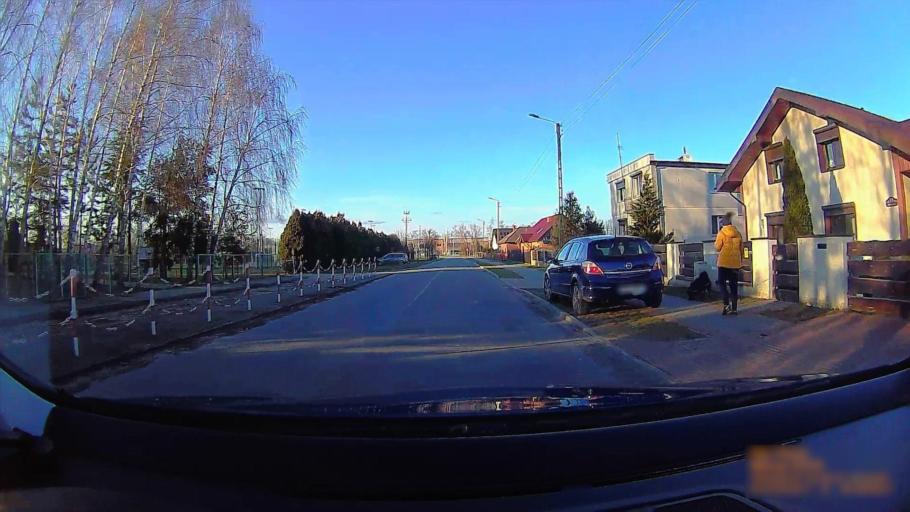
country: PL
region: Greater Poland Voivodeship
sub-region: Powiat koninski
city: Rychwal
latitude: 52.0743
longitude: 18.1662
